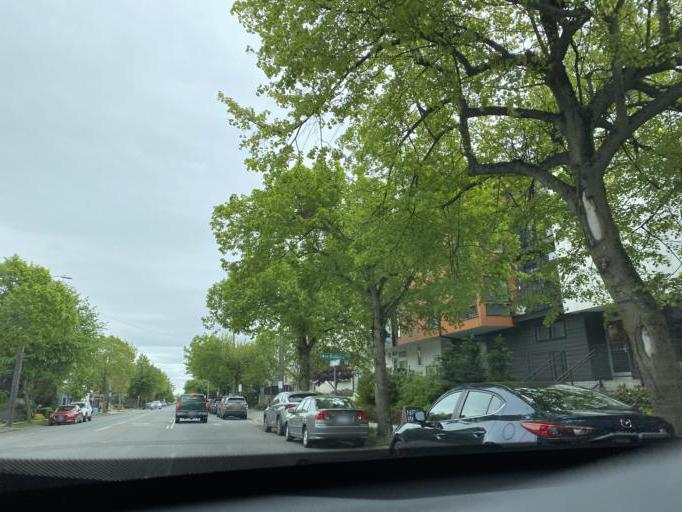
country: US
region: Washington
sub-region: King County
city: White Center
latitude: 47.5695
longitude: -122.3868
